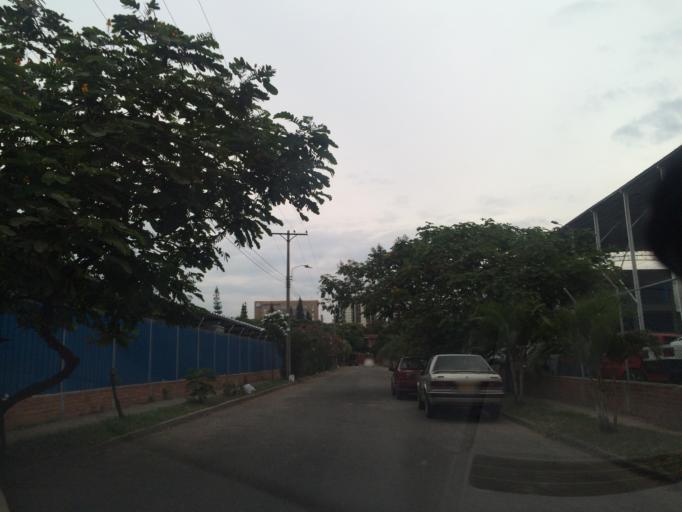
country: CO
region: Valle del Cauca
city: Cali
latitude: 3.4145
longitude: -76.5387
